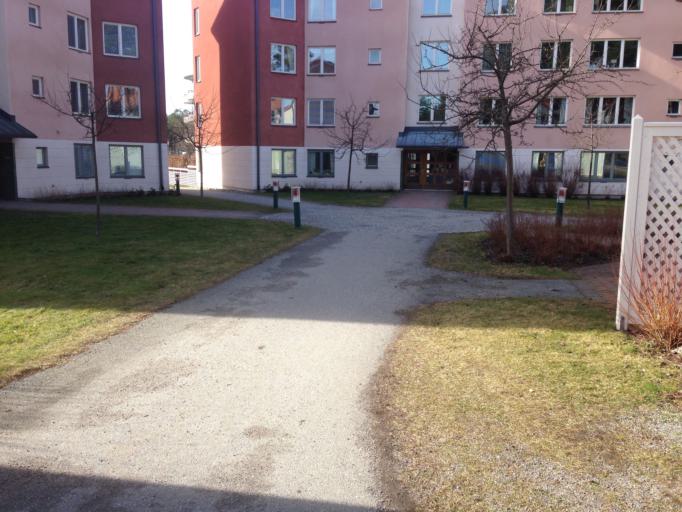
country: SE
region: Stockholm
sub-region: Vallentuna Kommun
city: Vallentuna
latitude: 59.5108
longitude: 18.0777
